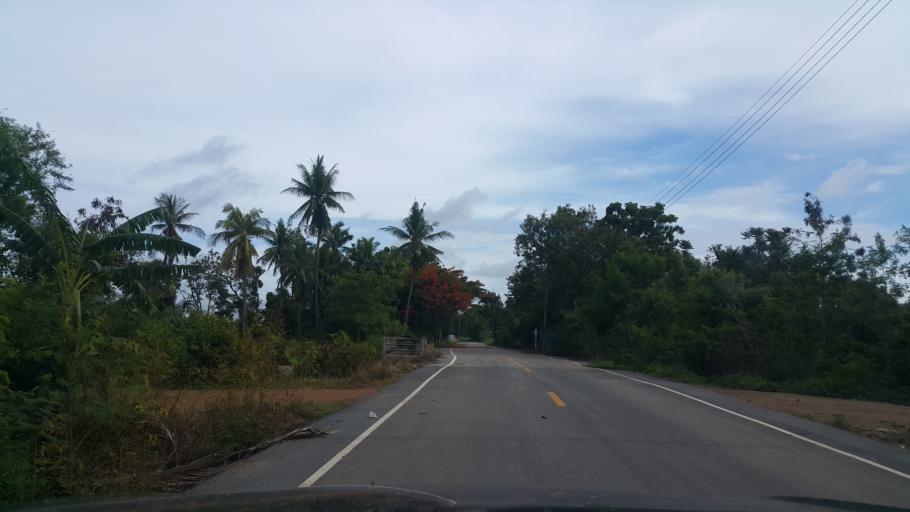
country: TH
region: Sukhothai
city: Si Nakhon
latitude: 17.2658
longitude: 99.9337
